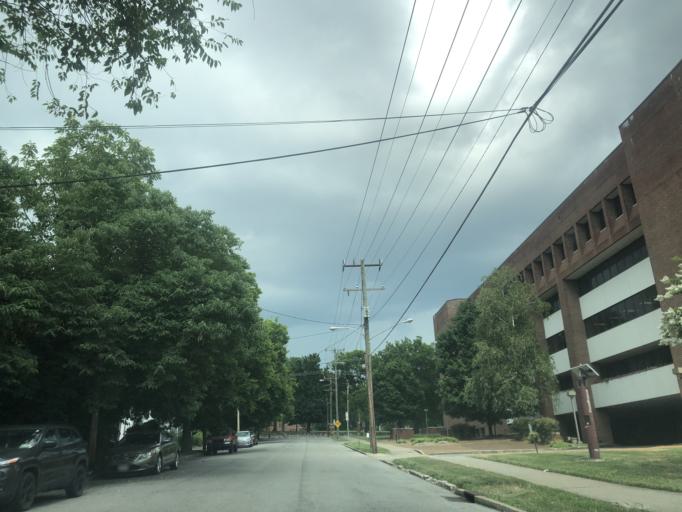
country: US
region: Tennessee
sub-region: Davidson County
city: Nashville
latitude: 36.1682
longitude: -86.8075
